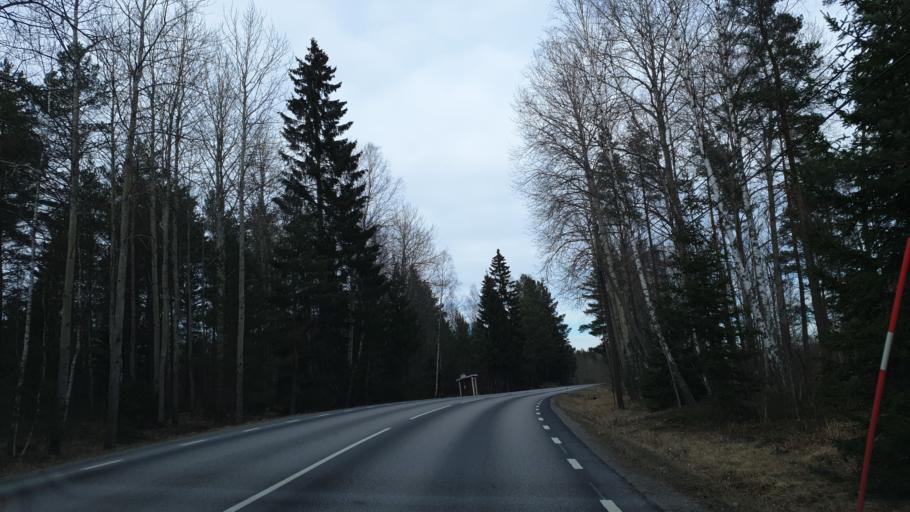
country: SE
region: Stockholm
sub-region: Osterakers Kommun
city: Akersberga
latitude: 59.5788
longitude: 18.2817
